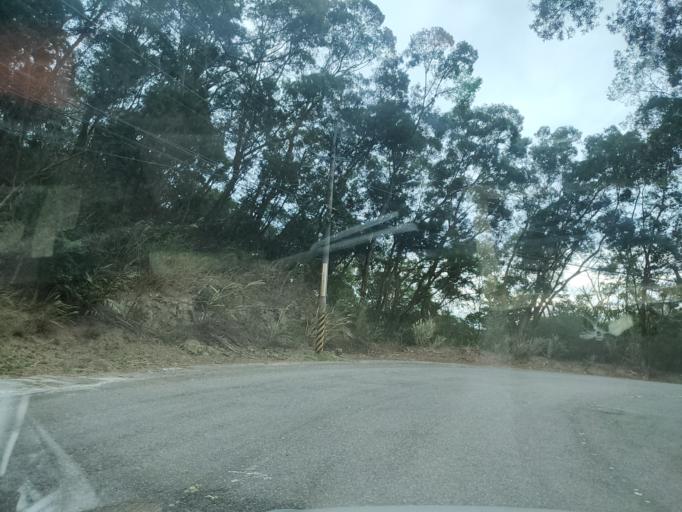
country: TW
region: Taiwan
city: Fengyuan
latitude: 24.3685
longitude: 120.7761
